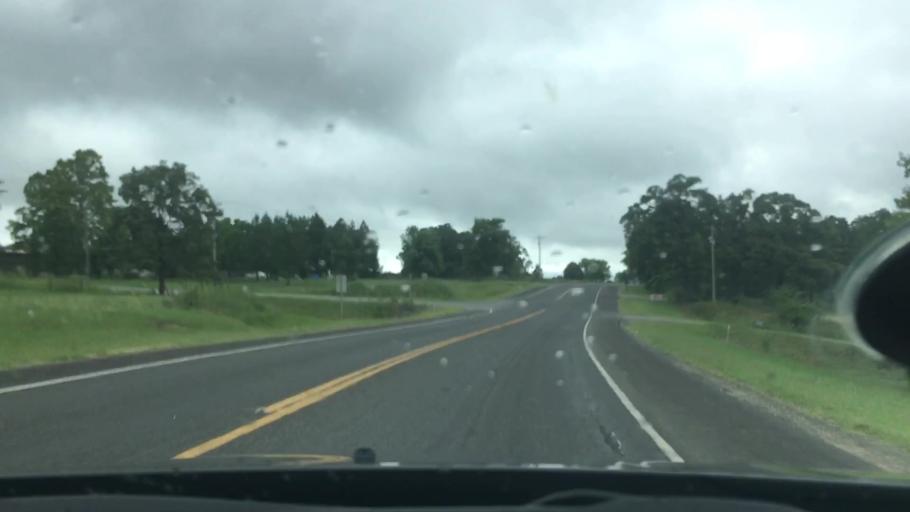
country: US
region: Oklahoma
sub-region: Sequoyah County
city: Vian
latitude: 35.5655
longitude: -94.9844
